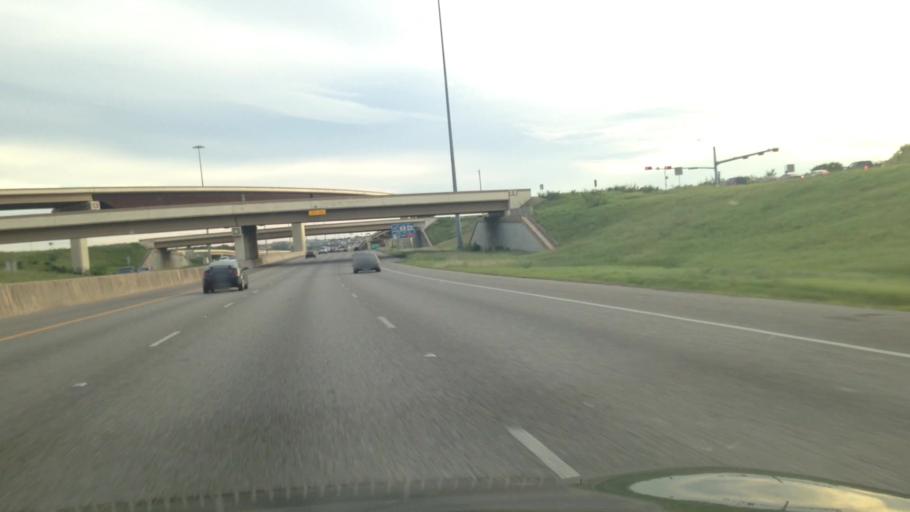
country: US
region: Texas
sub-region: Travis County
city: Onion Creek
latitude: 30.1136
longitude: -97.8067
